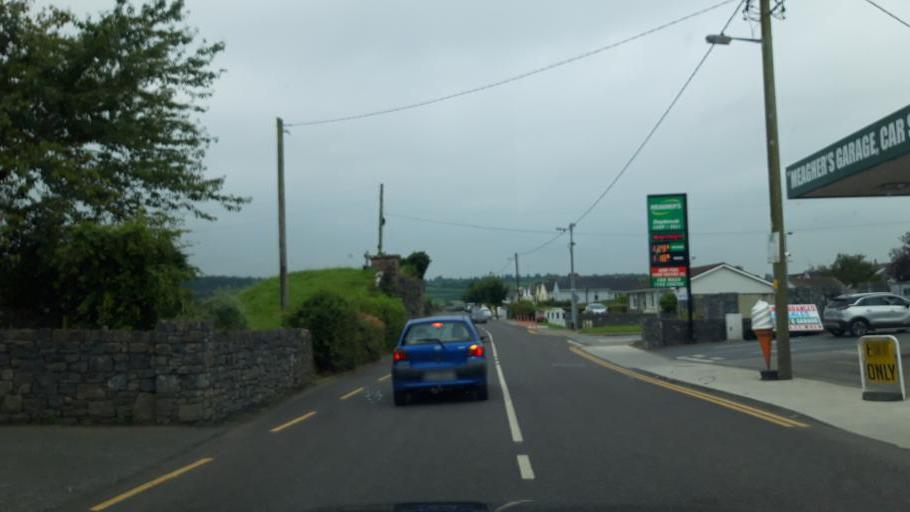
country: IE
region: Munster
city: Fethard
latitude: 52.4645
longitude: -7.7002
